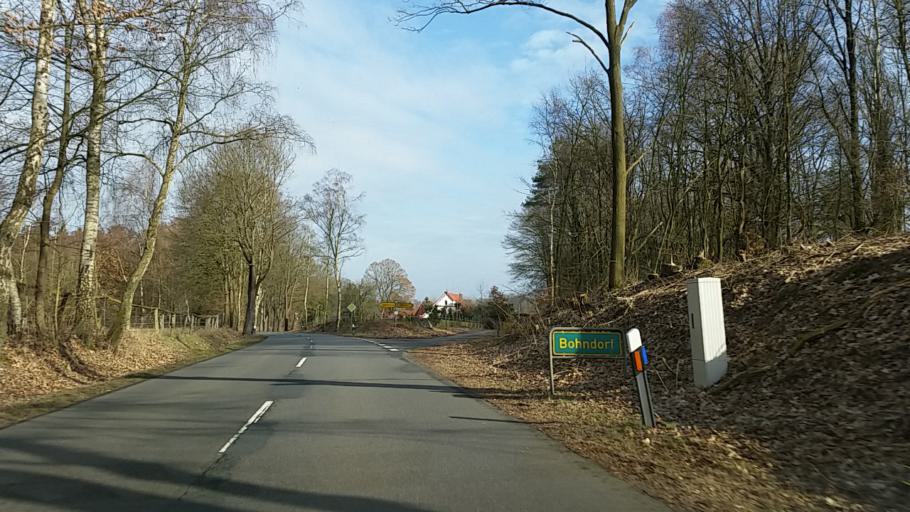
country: DE
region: Lower Saxony
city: Altenmedingen
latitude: 53.1732
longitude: 10.6255
